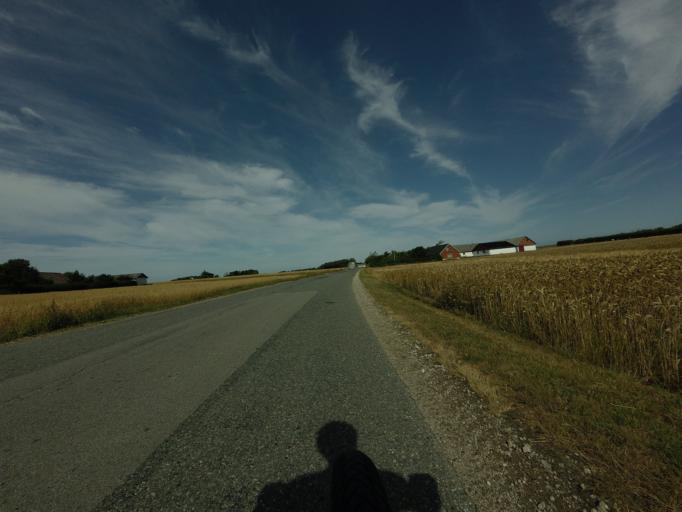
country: DK
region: North Denmark
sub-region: Hjorring Kommune
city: Vra
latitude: 57.4154
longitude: 9.8675
